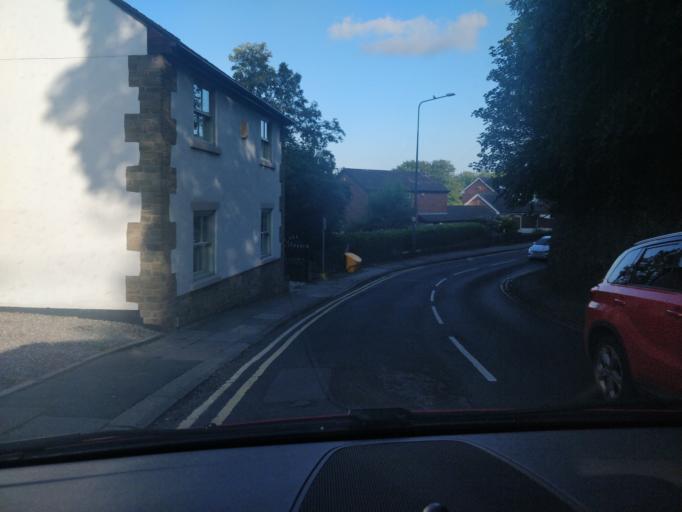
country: GB
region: England
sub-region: Lancashire
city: Appley Bridge
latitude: 53.5410
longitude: -2.7230
